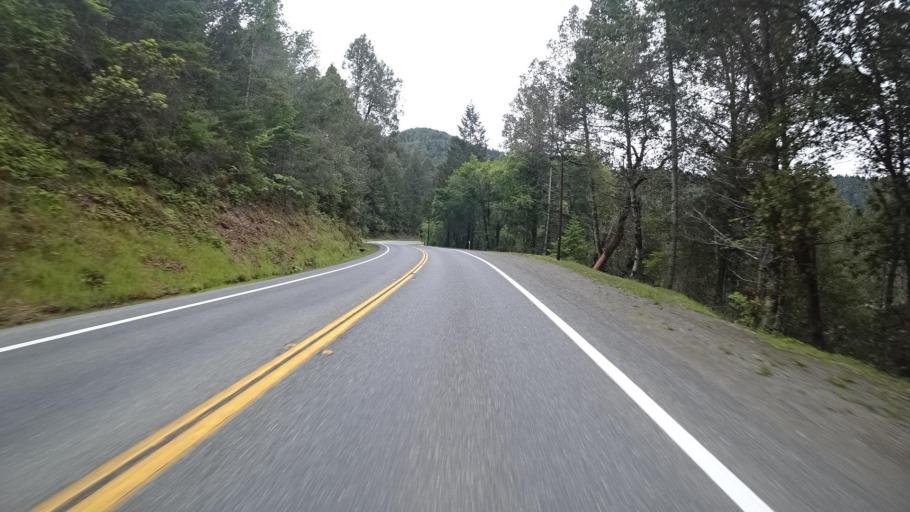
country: US
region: California
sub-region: Humboldt County
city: Willow Creek
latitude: 40.9987
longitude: -123.6428
